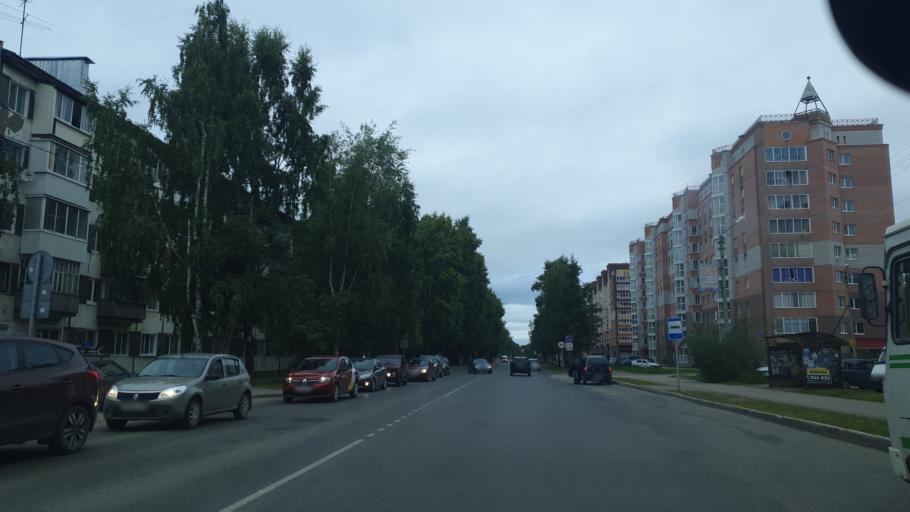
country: RU
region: Komi Republic
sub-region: Syktyvdinskiy Rayon
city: Syktyvkar
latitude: 61.6544
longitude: 50.7974
